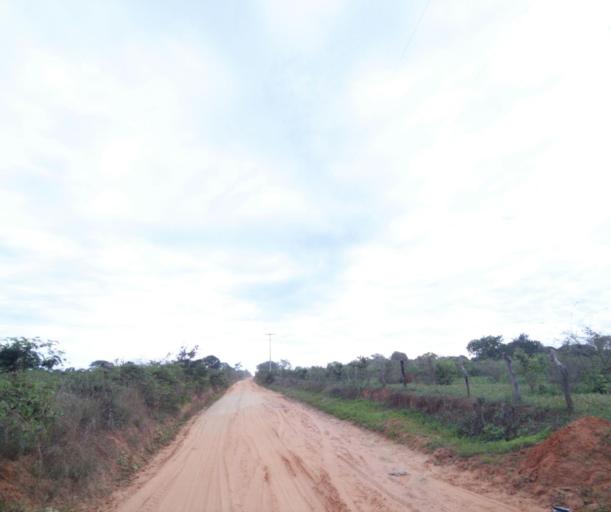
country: BR
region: Bahia
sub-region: Carinhanha
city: Carinhanha
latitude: -14.1811
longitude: -44.5180
